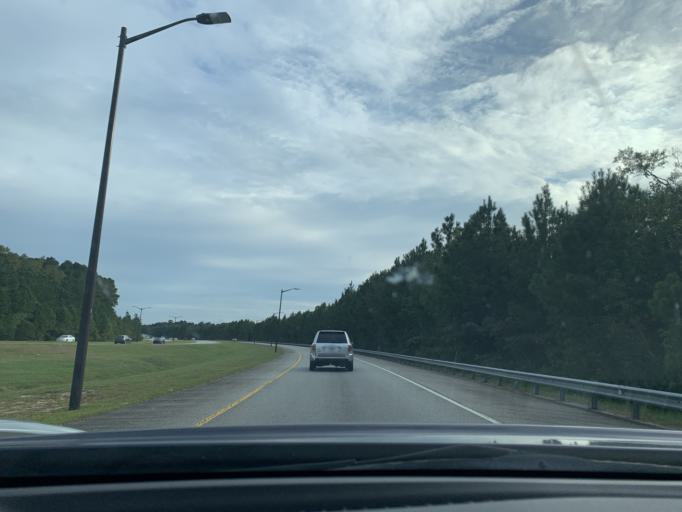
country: US
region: Georgia
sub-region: Chatham County
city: Pooler
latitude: 32.1193
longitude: -81.2696
